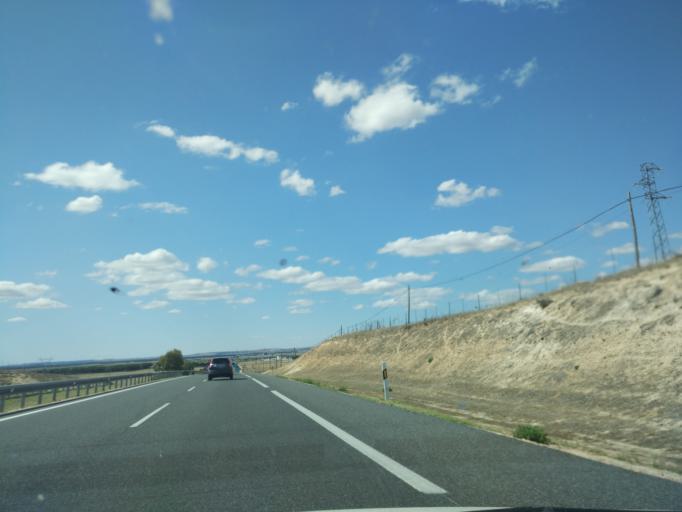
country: ES
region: Castille and Leon
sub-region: Provincia de Valladolid
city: San Vicente del Palacio
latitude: 41.2072
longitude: -4.8293
